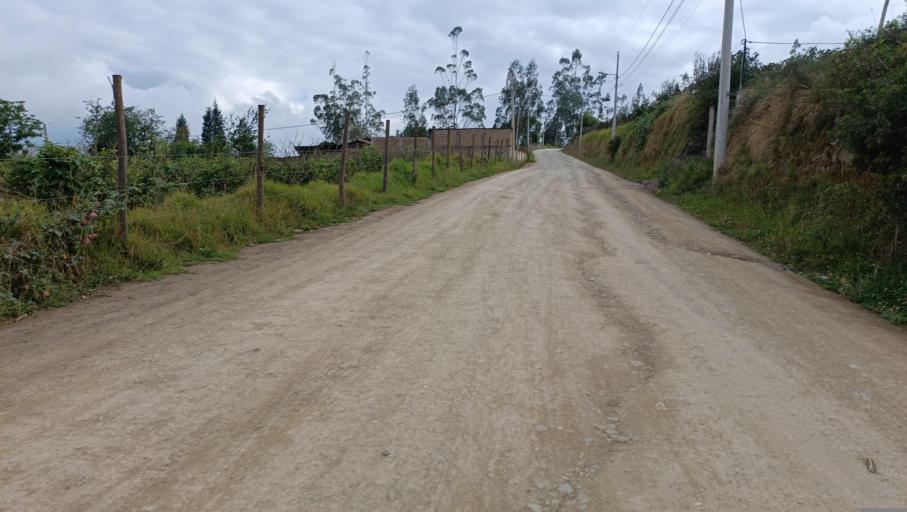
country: EC
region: Chimborazo
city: Guano
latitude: -1.6570
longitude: -78.5653
